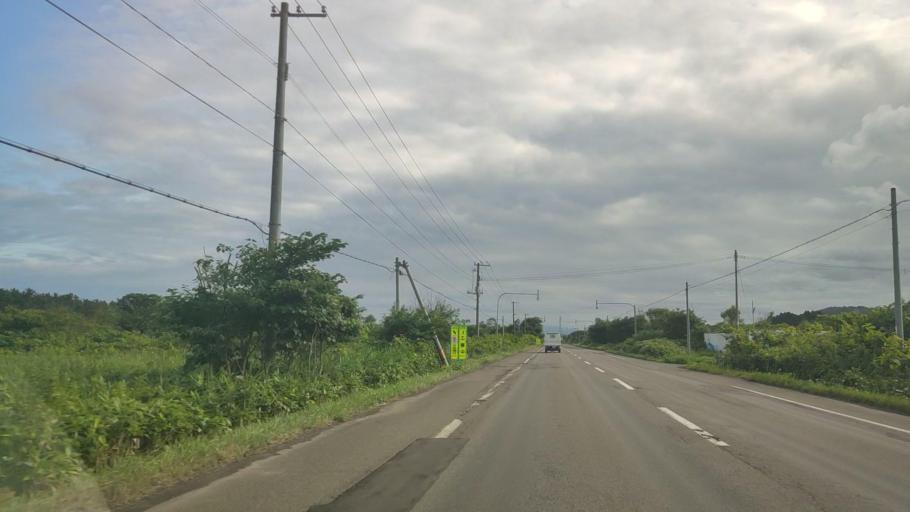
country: JP
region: Hokkaido
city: Niseko Town
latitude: 42.4653
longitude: 140.3395
